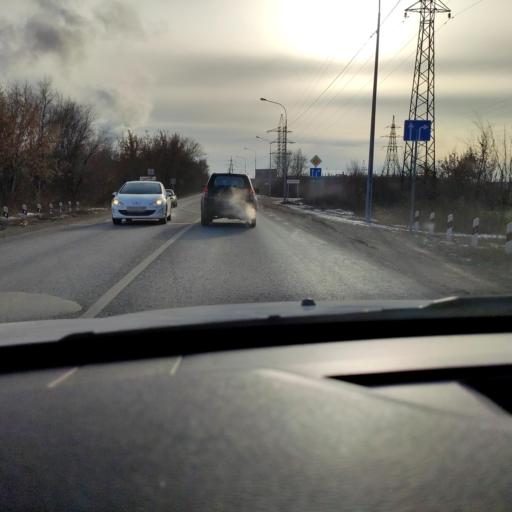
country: RU
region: Samara
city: Smyshlyayevka
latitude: 53.2681
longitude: 50.3861
